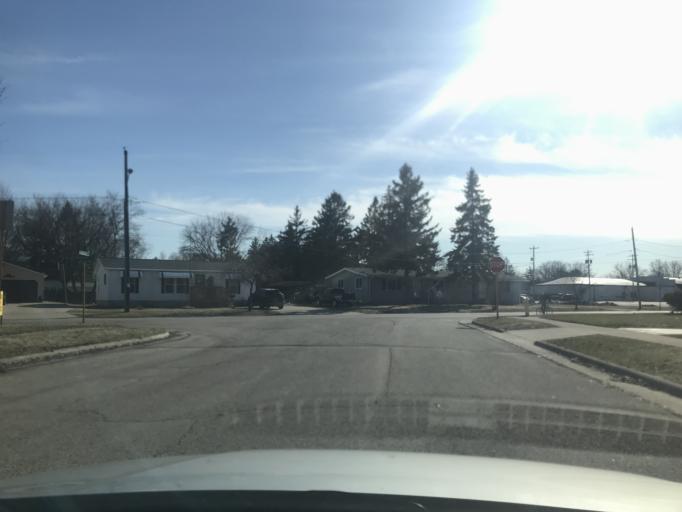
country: US
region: Wisconsin
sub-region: Marinette County
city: Marinette
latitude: 45.0930
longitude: -87.6453
